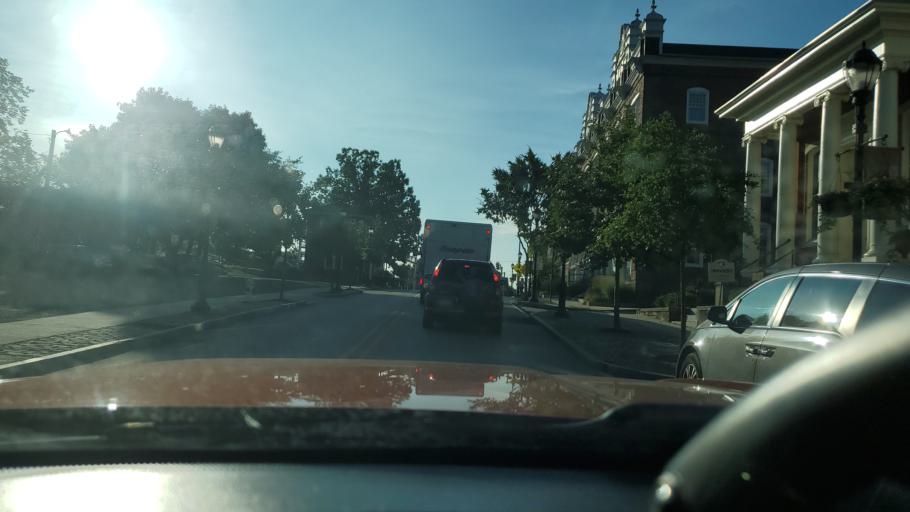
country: US
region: Pennsylvania
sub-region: Montgomery County
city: Souderton
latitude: 40.3100
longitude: -75.3220
